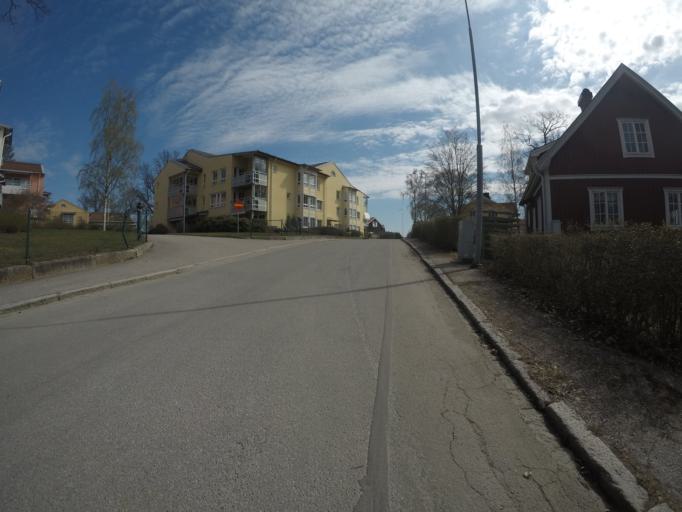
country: SE
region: Vaestmanland
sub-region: Vasteras
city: Vasteras
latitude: 59.6184
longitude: 16.5330
